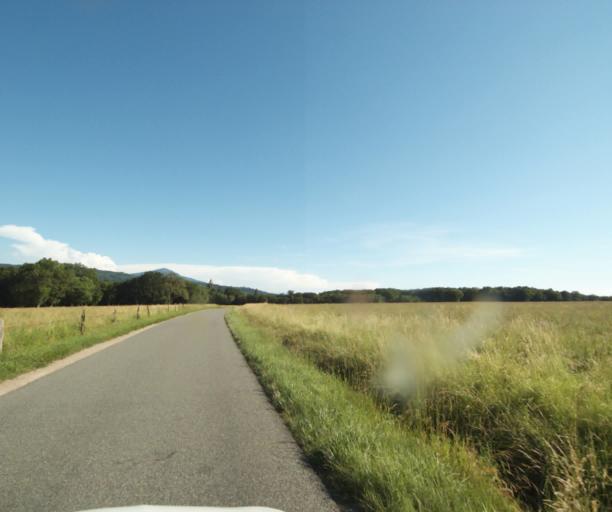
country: FR
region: Rhone-Alpes
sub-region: Departement de la Haute-Savoie
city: Massongy
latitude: 46.3430
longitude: 6.3285
